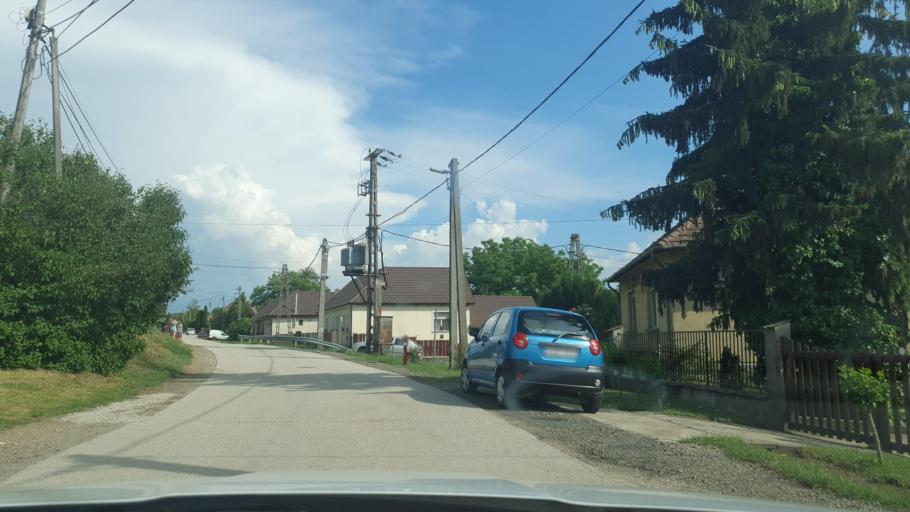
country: HU
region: Pest
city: Kosd
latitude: 47.7931
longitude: 19.2232
